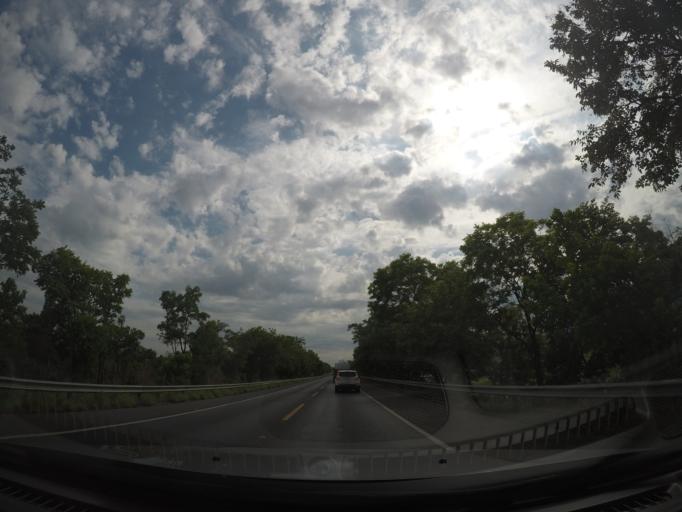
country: BR
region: Goias
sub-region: Formosa
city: Formosa
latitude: -14.9172
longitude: -46.9550
